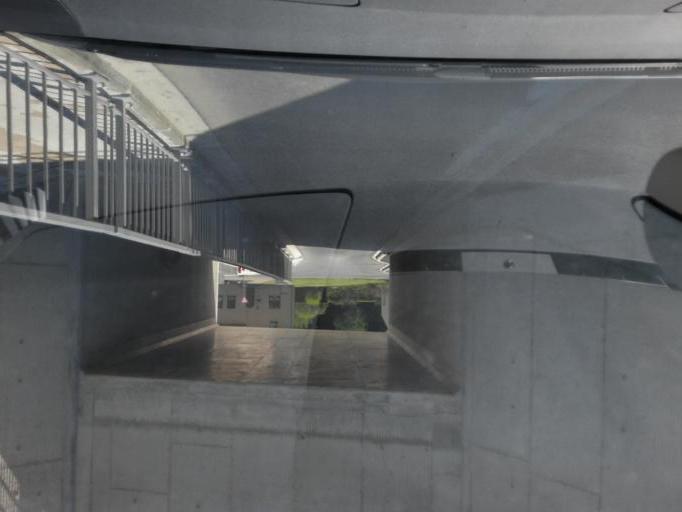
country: BE
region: Wallonia
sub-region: Province du Luxembourg
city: Arlon
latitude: 49.6900
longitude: 5.7764
